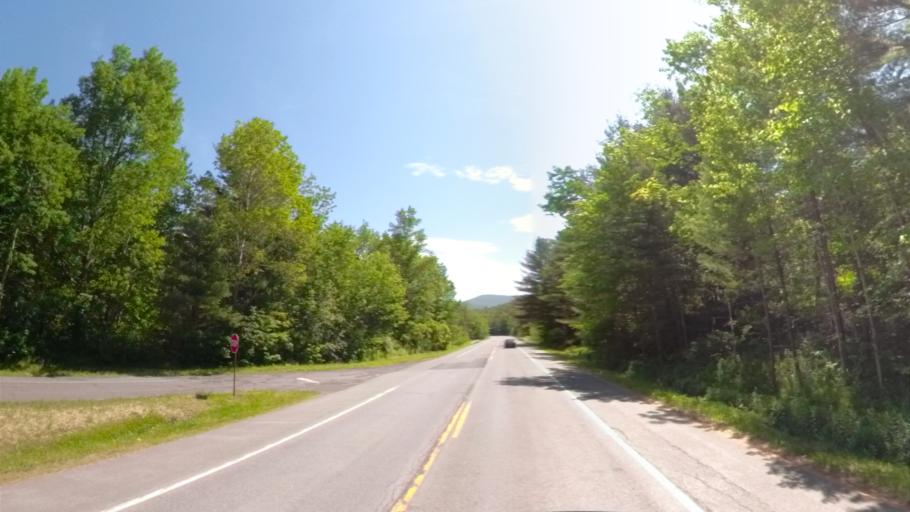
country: US
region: New York
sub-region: Ulster County
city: Shokan
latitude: 42.1155
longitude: -74.4121
